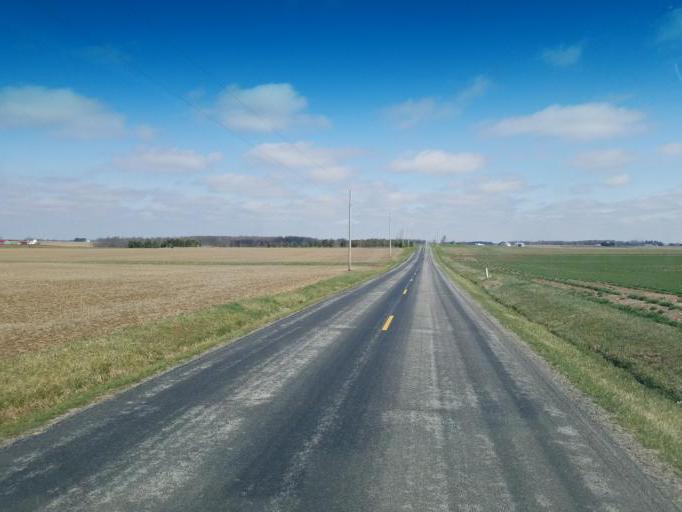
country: US
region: Ohio
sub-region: Crawford County
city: Bucyrus
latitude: 40.8805
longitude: -82.9018
